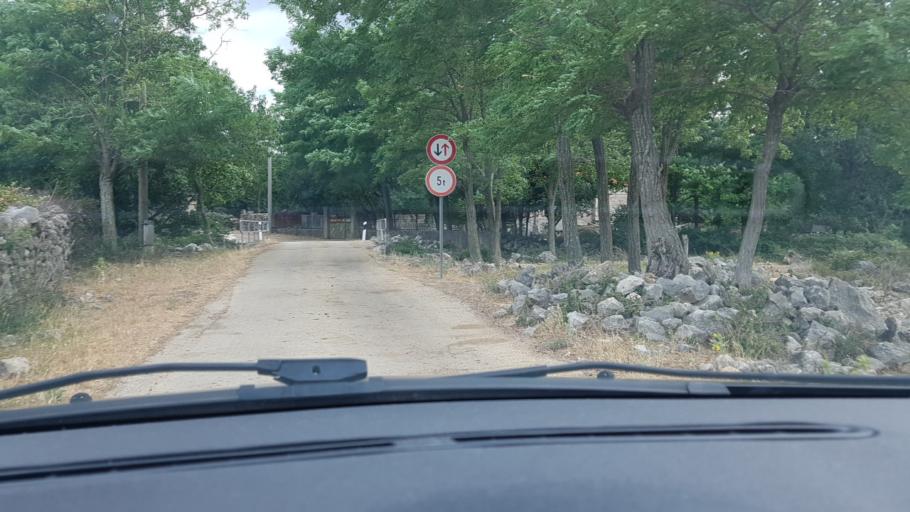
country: HR
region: Zadarska
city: Gracac
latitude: 44.1919
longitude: 15.9088
